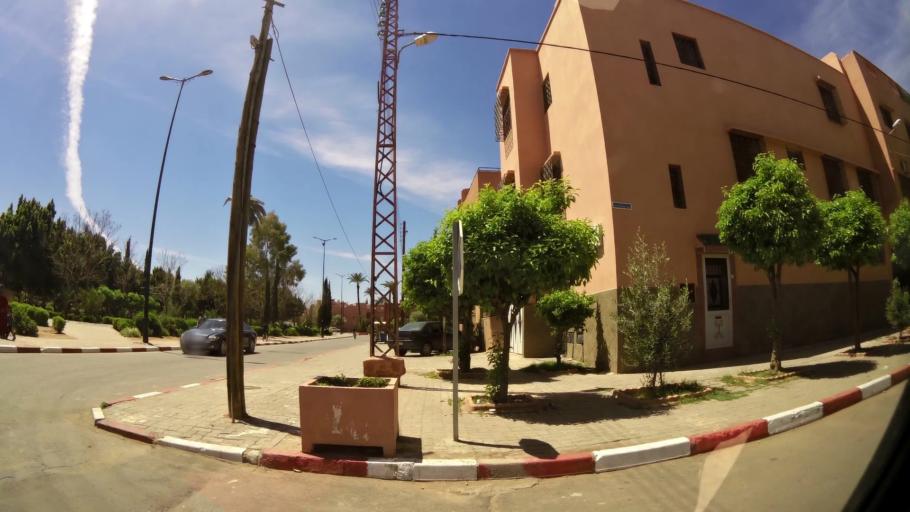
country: MA
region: Marrakech-Tensift-Al Haouz
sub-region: Marrakech
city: Marrakesh
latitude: 31.6566
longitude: -7.9975
